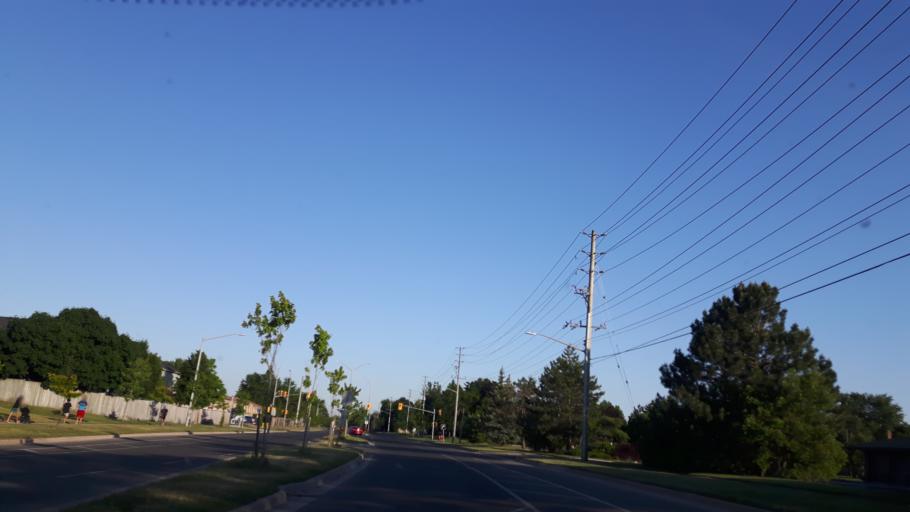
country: CA
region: Ontario
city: London
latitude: 42.9432
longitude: -81.2142
